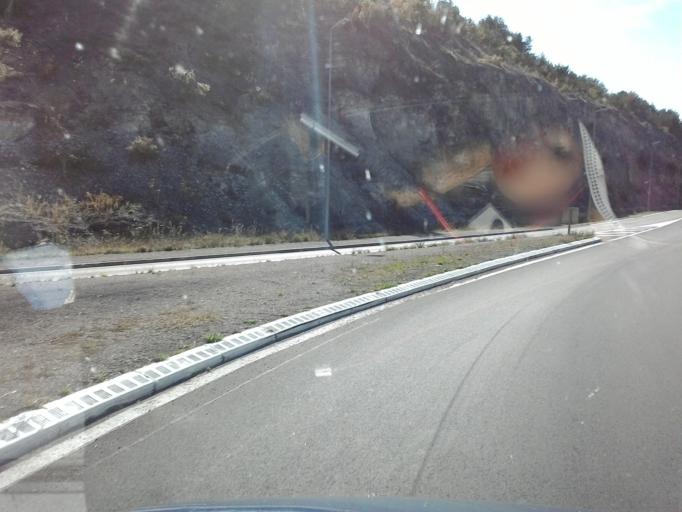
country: FR
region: Bourgogne
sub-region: Departement de l'Yonne
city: Tonnerre
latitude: 47.8508
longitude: 3.9906
